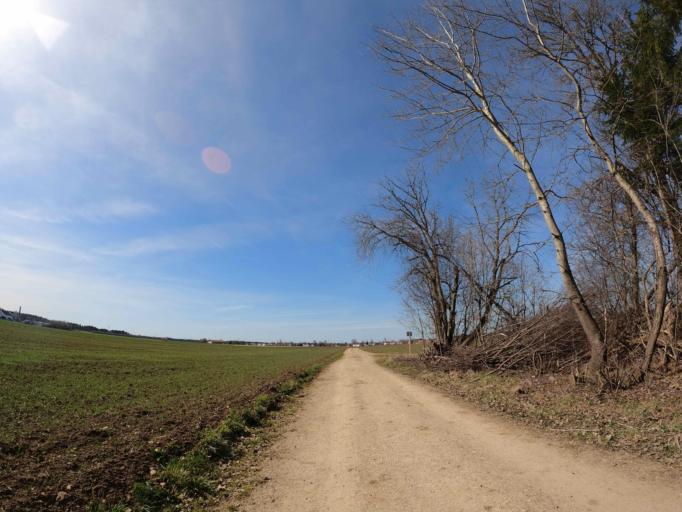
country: DE
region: Bavaria
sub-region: Upper Bavaria
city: Brunnthal
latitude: 48.0001
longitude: 11.6957
